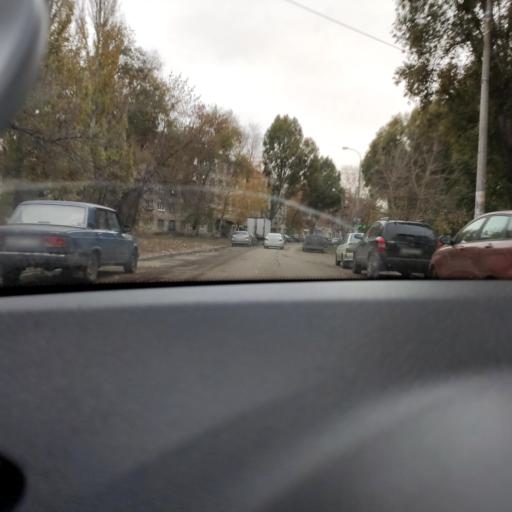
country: RU
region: Samara
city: Petra-Dubrava
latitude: 53.2318
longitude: 50.2799
